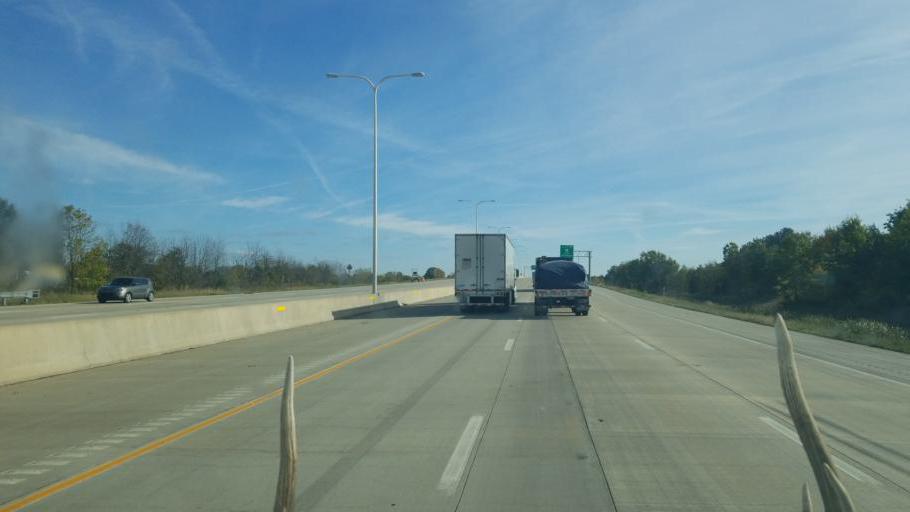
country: US
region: Illinois
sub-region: Effingham County
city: Effingham
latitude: 39.1437
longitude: -88.5412
